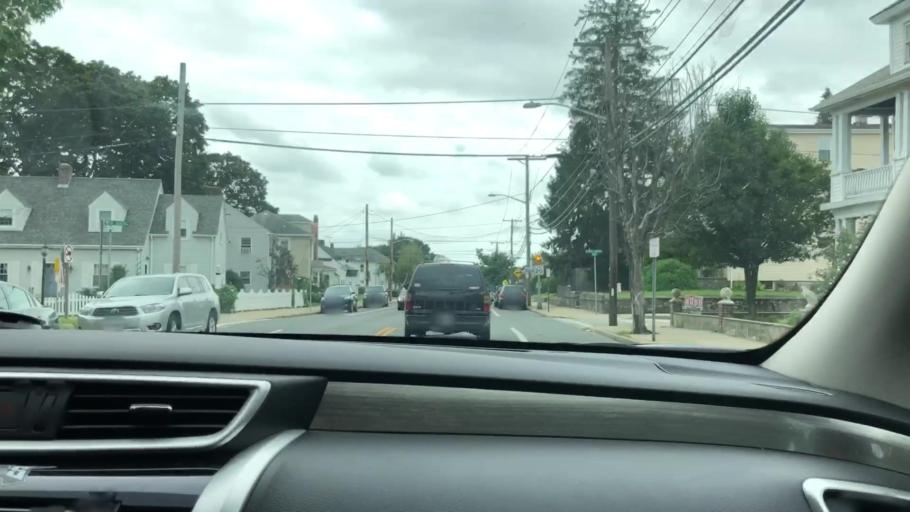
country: US
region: Rhode Island
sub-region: Providence County
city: Central Falls
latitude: 41.8702
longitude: -71.4136
